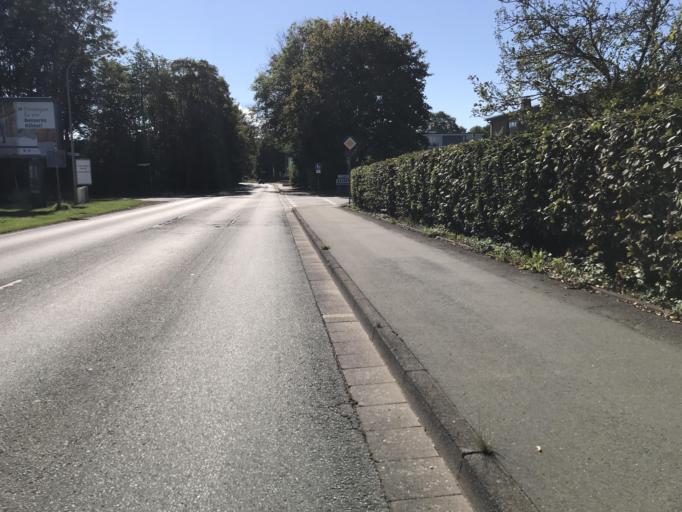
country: DE
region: Hesse
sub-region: Regierungsbezirk Kassel
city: Korbach
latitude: 51.2648
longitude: 8.8810
